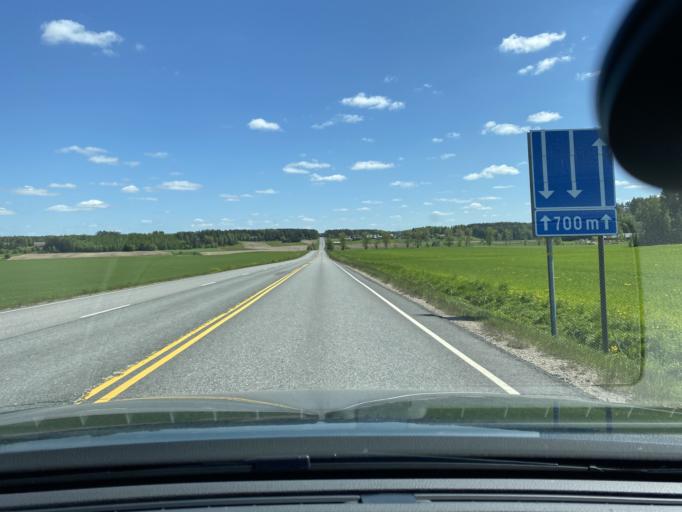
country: FI
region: Varsinais-Suomi
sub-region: Salo
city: Halikko
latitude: 60.3756
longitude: 22.9716
